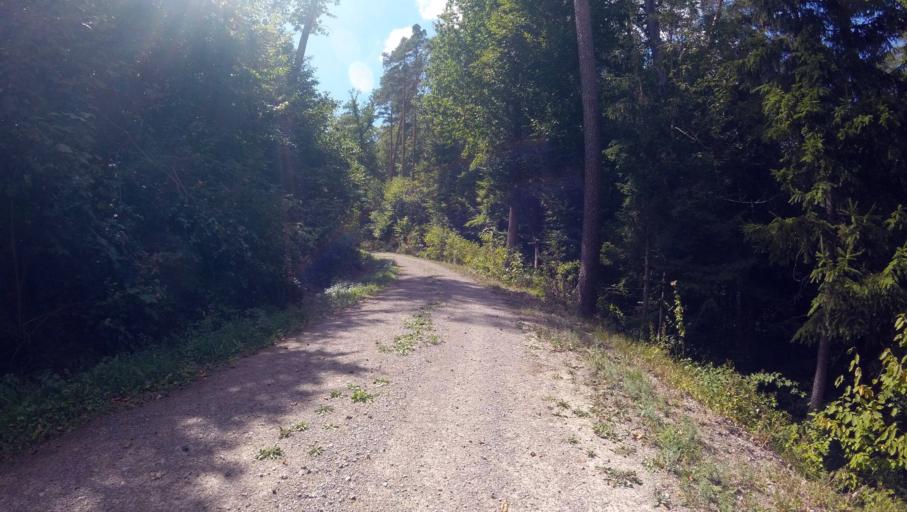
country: DE
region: Baden-Wuerttemberg
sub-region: Regierungsbezirk Stuttgart
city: Oppenweiler
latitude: 48.9934
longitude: 9.4399
